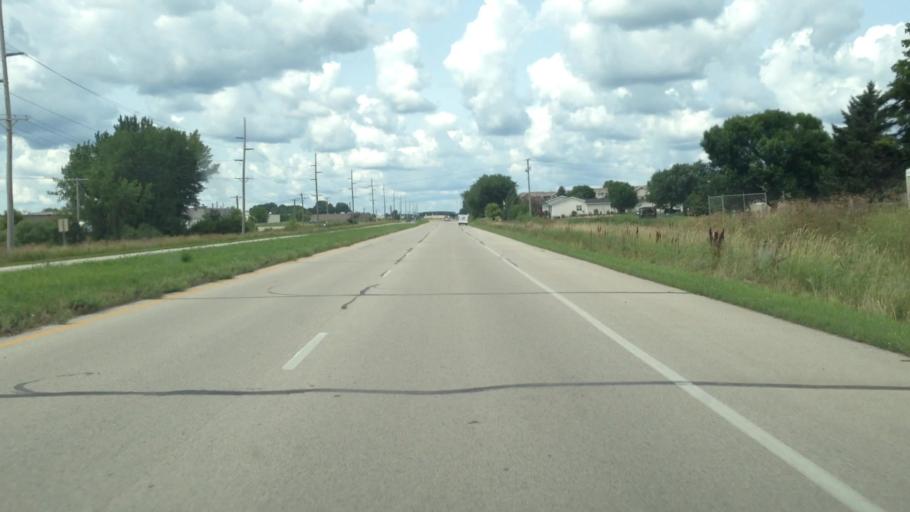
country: US
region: Minnesota
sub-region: Olmsted County
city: Rochester
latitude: 44.0456
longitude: -92.5046
